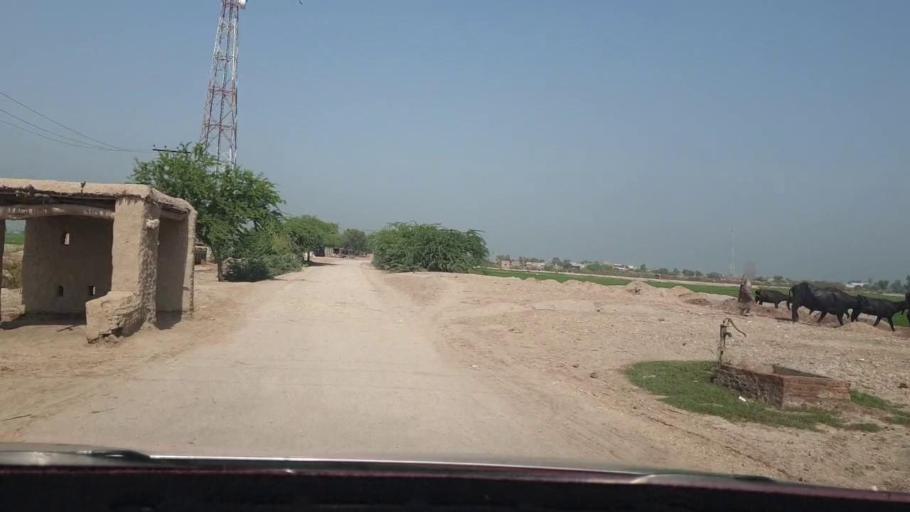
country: PK
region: Sindh
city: Nasirabad
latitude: 27.4192
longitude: 67.9306
